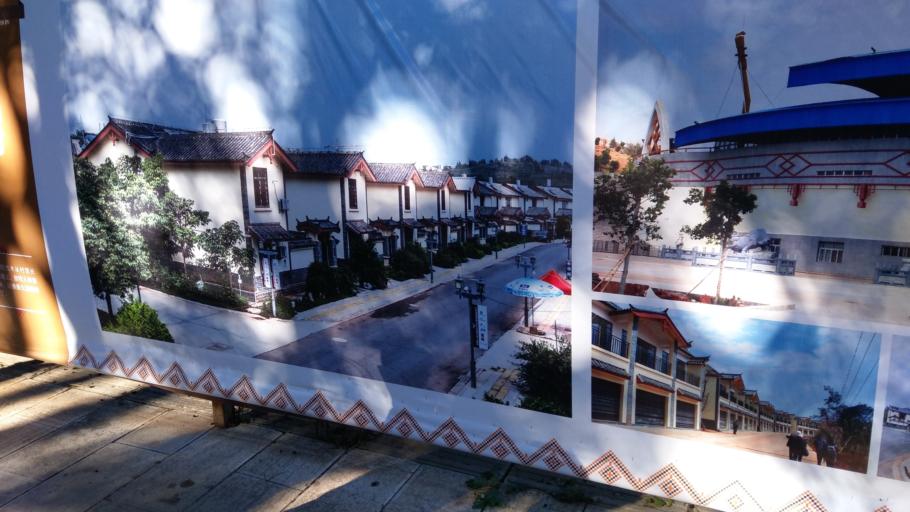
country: CN
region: Yunnan
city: Shilin
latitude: 24.8261
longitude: 103.3227
